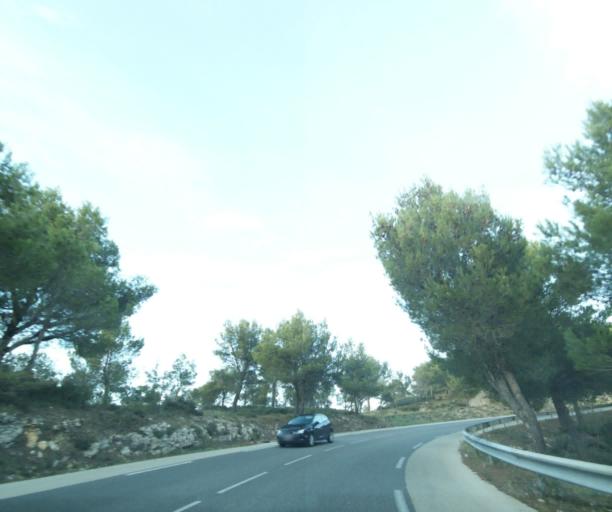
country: FR
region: Provence-Alpes-Cote d'Azur
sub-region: Departement des Bouches-du-Rhone
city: Roquefort-la-Bedoule
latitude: 43.2333
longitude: 5.5886
